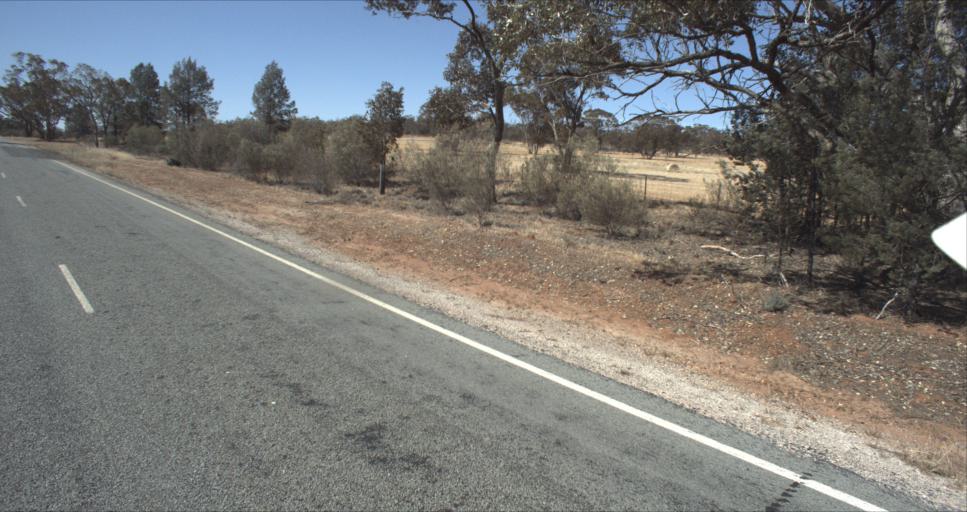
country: AU
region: New South Wales
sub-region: Leeton
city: Leeton
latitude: -34.4809
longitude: 146.4342
